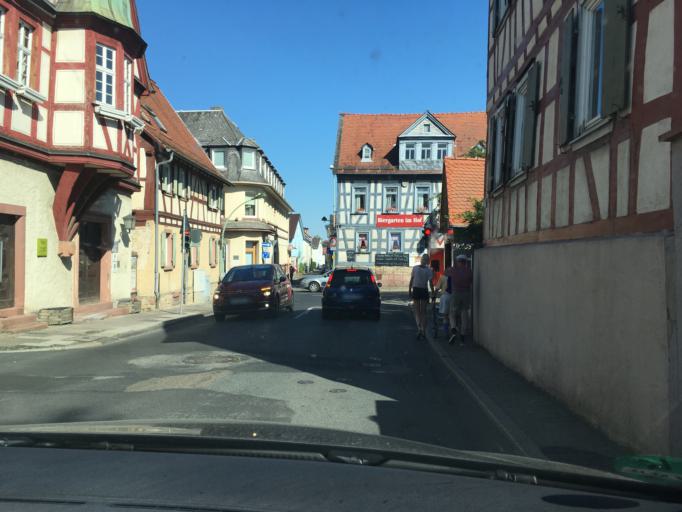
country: DE
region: Hesse
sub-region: Regierungsbezirk Darmstadt
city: Bad Vilbel
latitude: 50.1449
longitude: 8.7266
